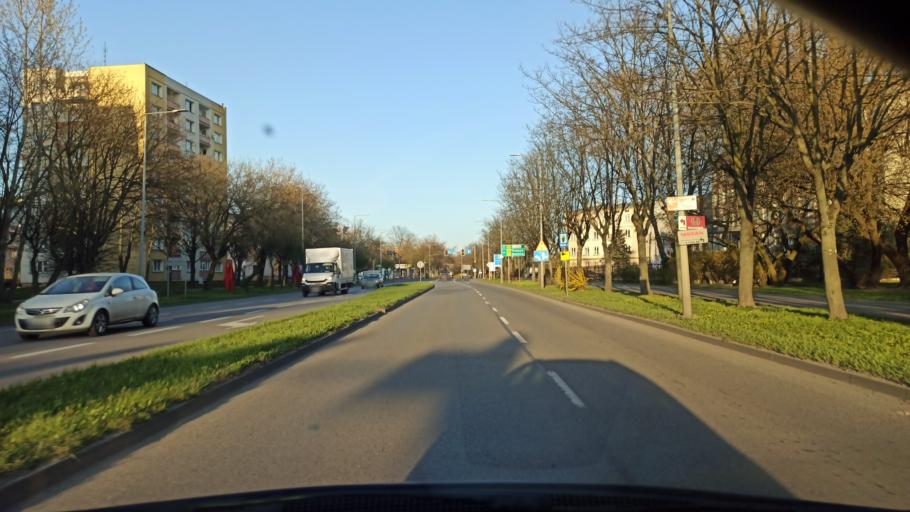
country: PL
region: Warmian-Masurian Voivodeship
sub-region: Powiat elblaski
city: Elblag
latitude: 54.1559
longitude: 19.4020
